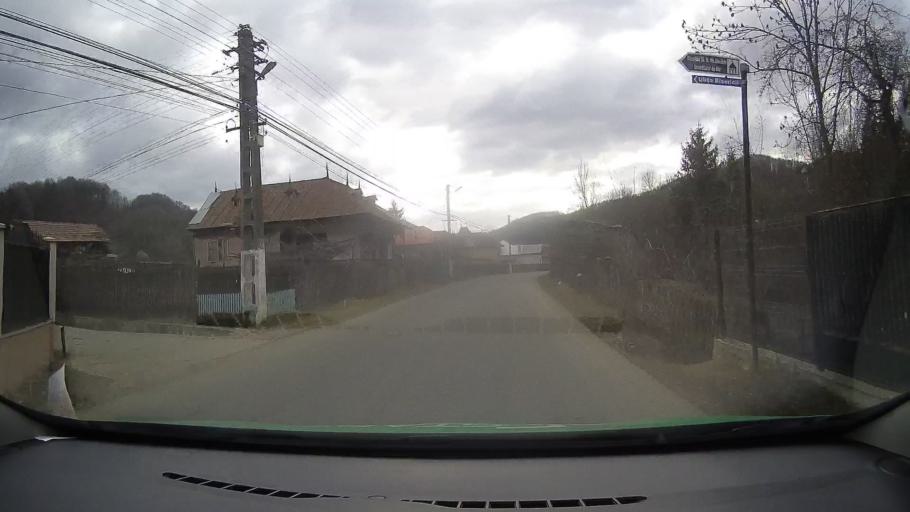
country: RO
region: Dambovita
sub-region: Comuna Visinesti
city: Visinesti
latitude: 45.1089
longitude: 25.5519
